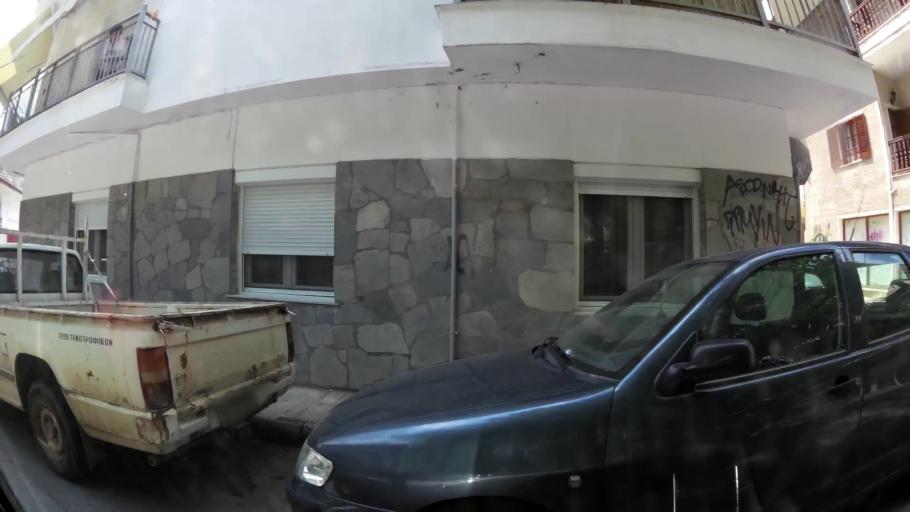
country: GR
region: West Macedonia
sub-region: Nomos Kozanis
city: Kozani
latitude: 40.3038
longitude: 21.7864
